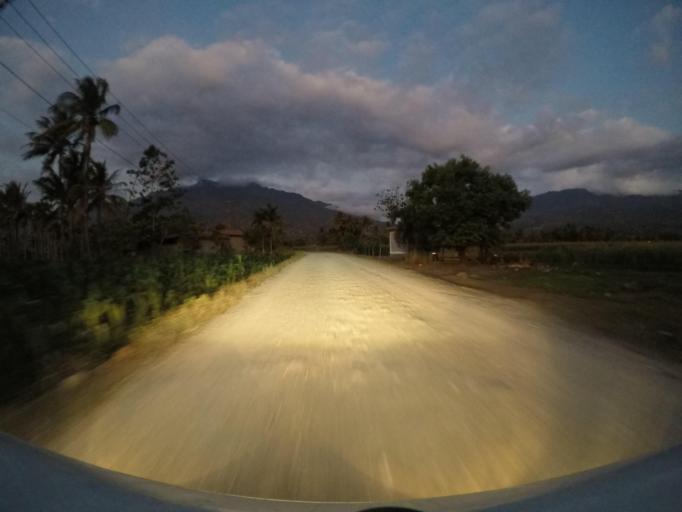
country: TL
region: Bobonaro
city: Maliana
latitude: -8.9807
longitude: 125.2153
